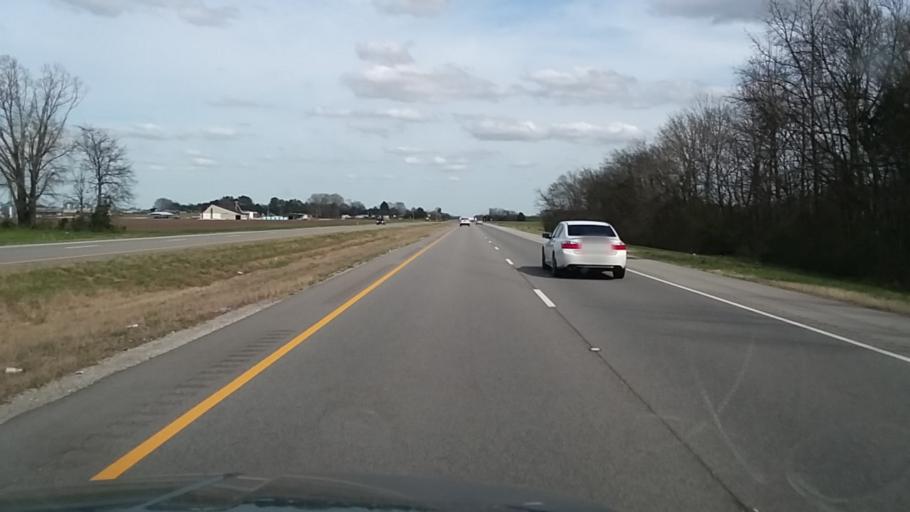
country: US
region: Alabama
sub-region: Colbert County
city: Muscle Shoals
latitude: 34.6848
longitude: -87.5739
